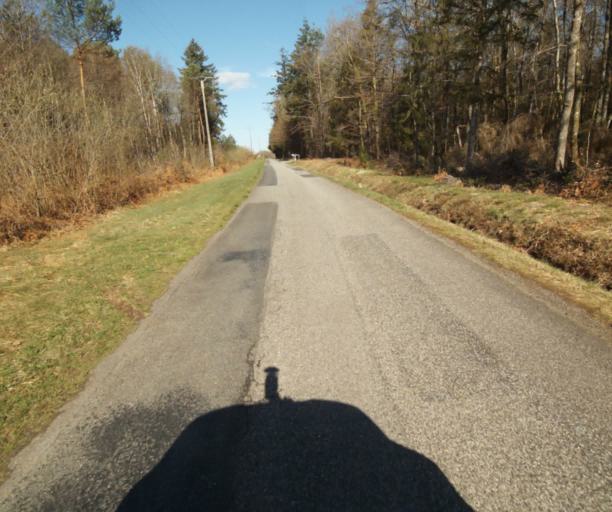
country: FR
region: Limousin
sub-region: Departement de la Correze
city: Correze
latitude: 45.2536
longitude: 1.9225
